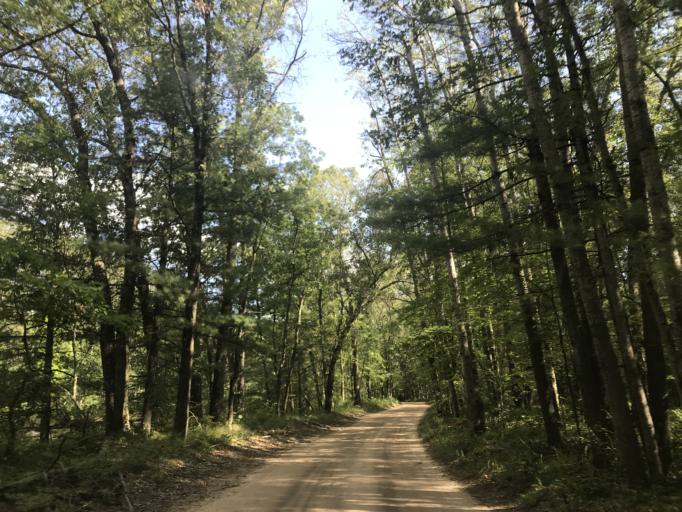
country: US
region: Michigan
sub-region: Newaygo County
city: Newaygo
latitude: 43.4631
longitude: -85.7641
